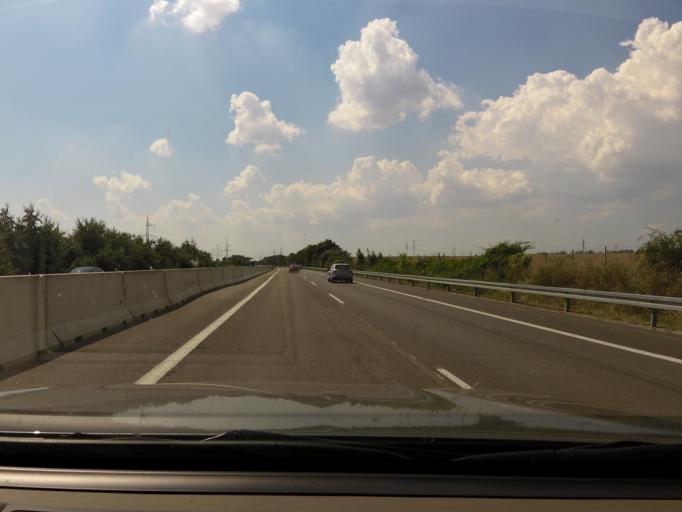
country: SK
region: Trnavsky
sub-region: Okres Trnava
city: Trnava
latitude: 48.3578
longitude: 17.6735
